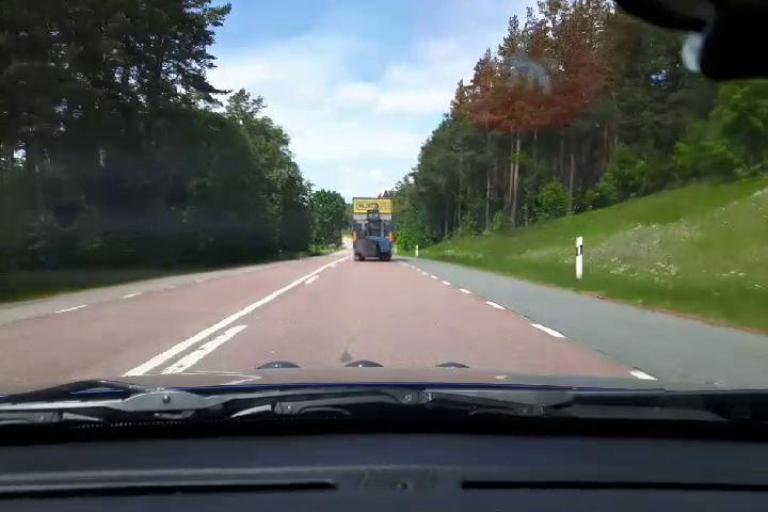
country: SE
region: Uppsala
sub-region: Osthammars Kommun
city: Bjorklinge
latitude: 60.1396
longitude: 17.5050
